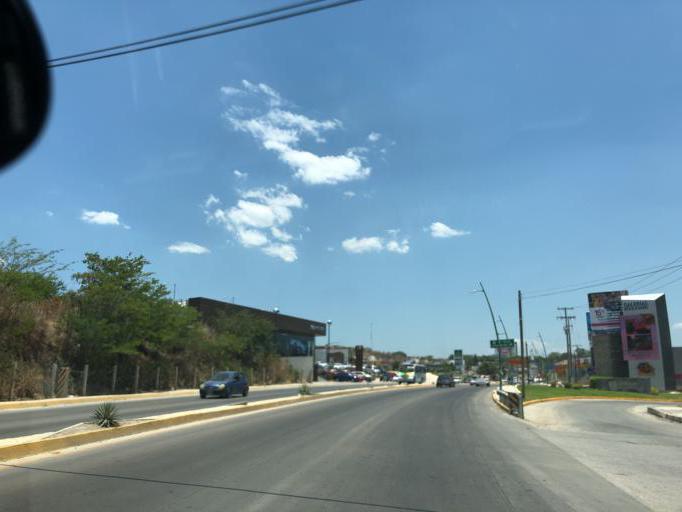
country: MX
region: Chiapas
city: Tuxtla Gutierrez
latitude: 16.7494
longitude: -93.1484
